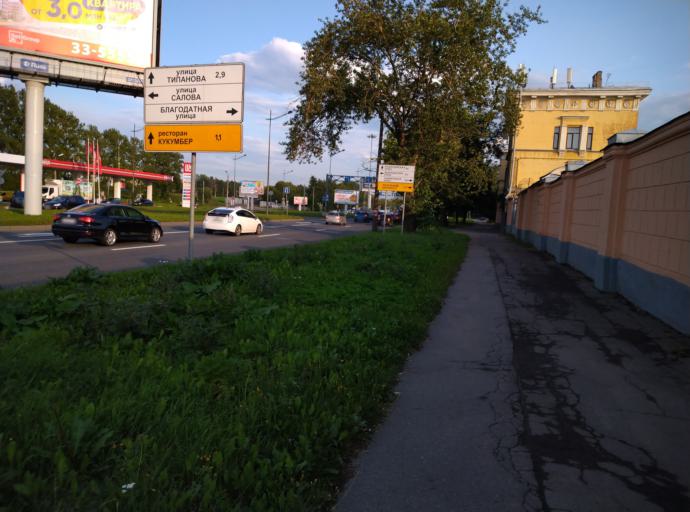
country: RU
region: St.-Petersburg
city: Kupchino
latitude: 59.8797
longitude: 30.3473
